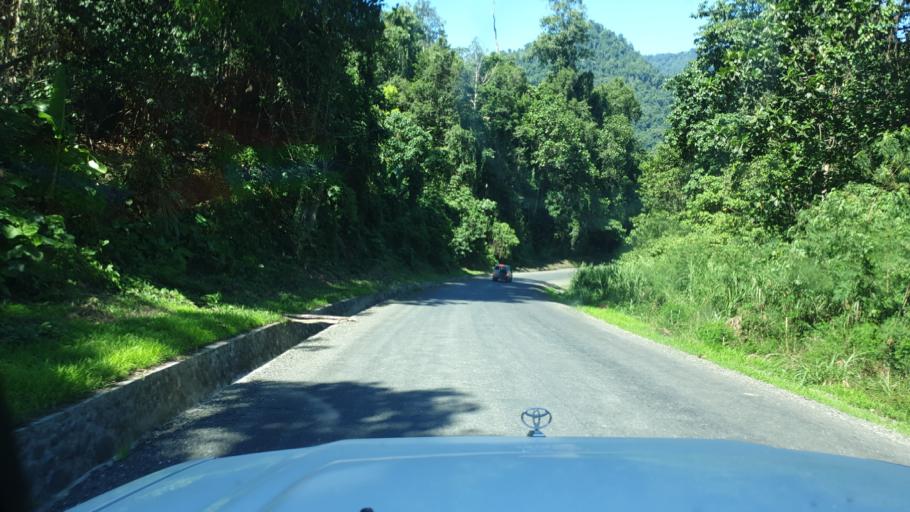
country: PG
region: Madang
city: Madang
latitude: -5.4343
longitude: 145.5505
